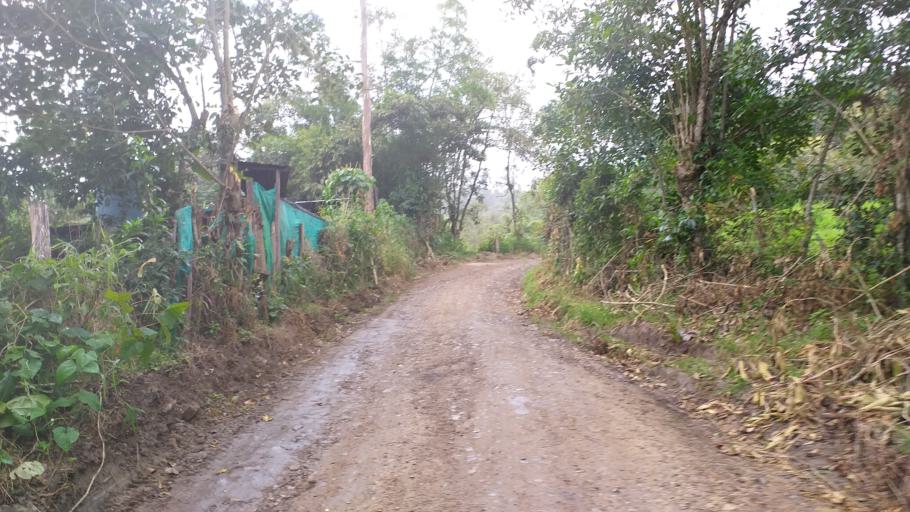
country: CO
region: Cundinamarca
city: Tenza
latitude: 5.0866
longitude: -73.4558
